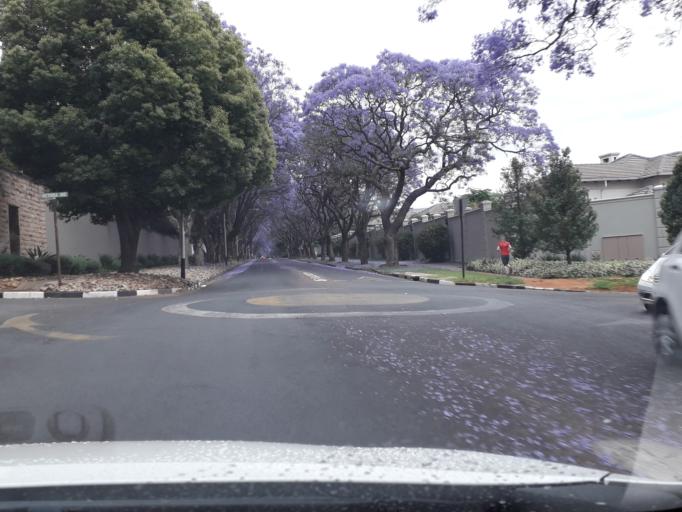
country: ZA
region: Gauteng
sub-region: City of Johannesburg Metropolitan Municipality
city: Johannesburg
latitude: -26.1427
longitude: 28.0507
